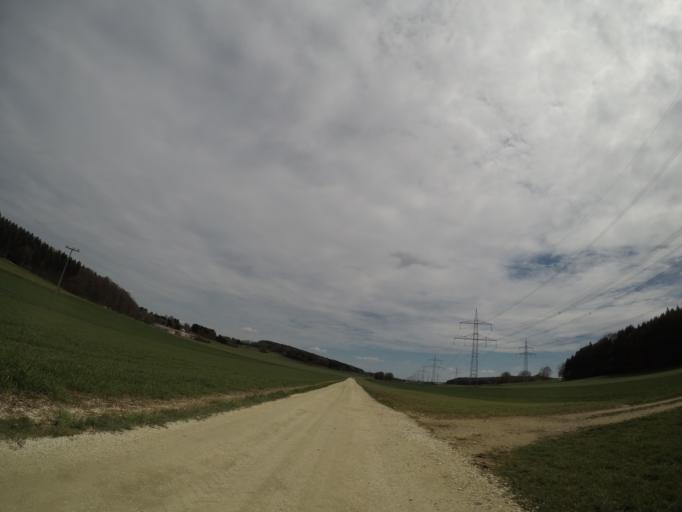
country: DE
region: Baden-Wuerttemberg
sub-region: Tuebingen Region
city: Laichingen
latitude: 48.4812
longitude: 9.6620
